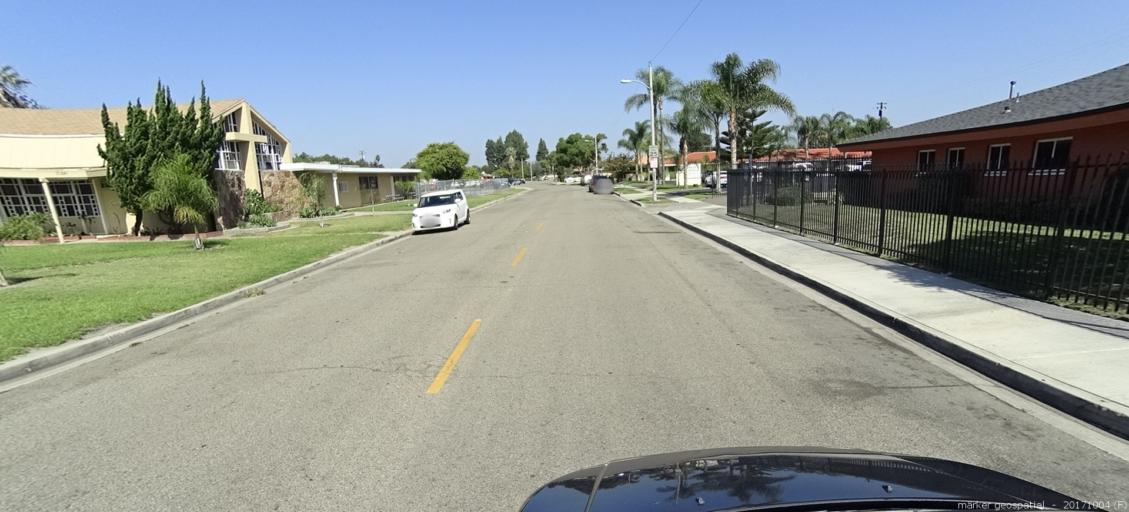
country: US
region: California
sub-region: Orange County
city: Garden Grove
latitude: 33.7889
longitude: -117.9537
